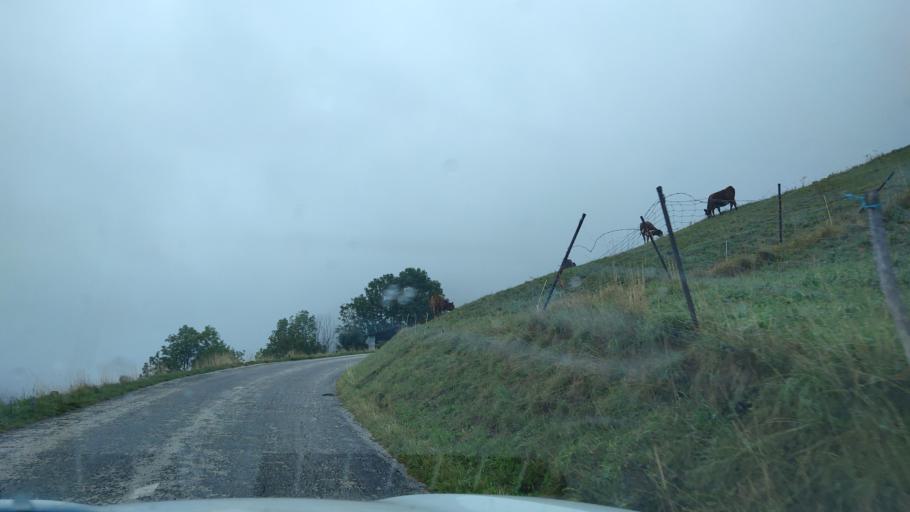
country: FR
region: Rhone-Alpes
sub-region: Departement de la Savoie
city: Modane
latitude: 45.2883
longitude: 6.8182
